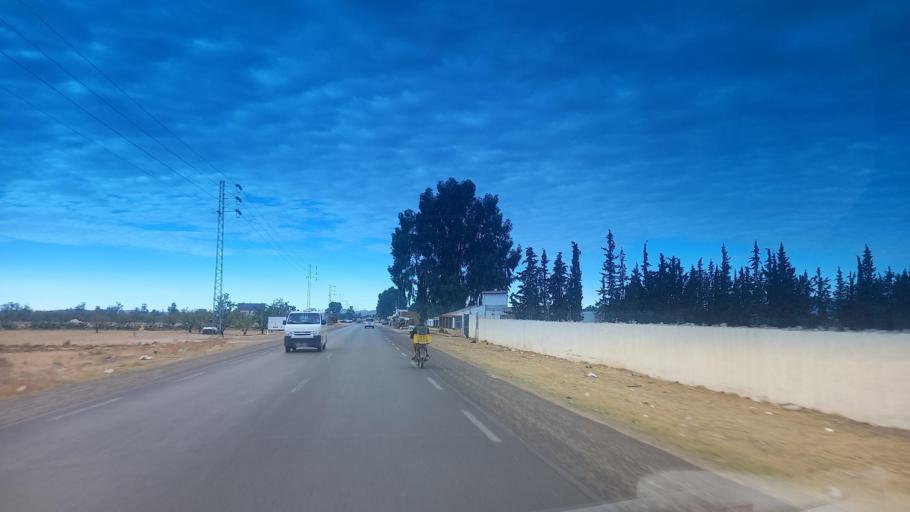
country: TN
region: Al Qasrayn
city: Kasserine
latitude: 35.2653
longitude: 9.0929
